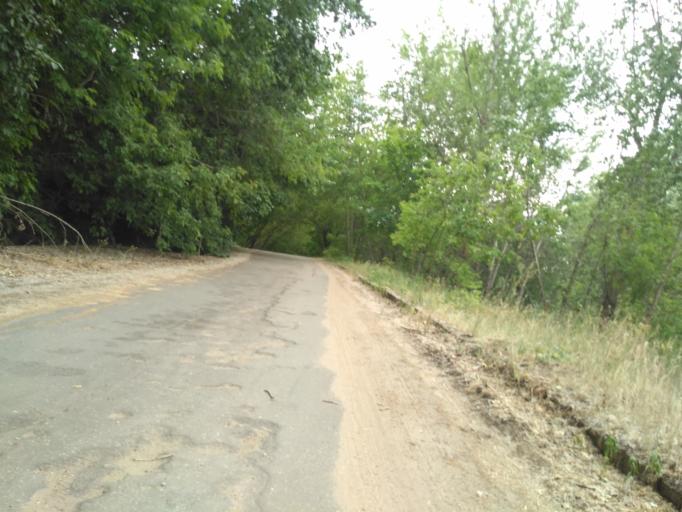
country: RU
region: Nizjnij Novgorod
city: Nizhniy Novgorod
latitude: 56.2956
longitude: 43.9674
